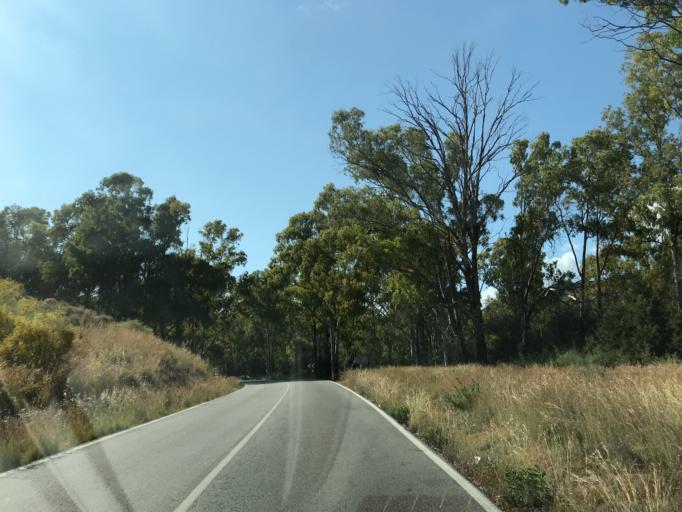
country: ES
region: Andalusia
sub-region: Provincia de Malaga
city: Benahavis
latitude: 36.5051
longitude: -5.0296
